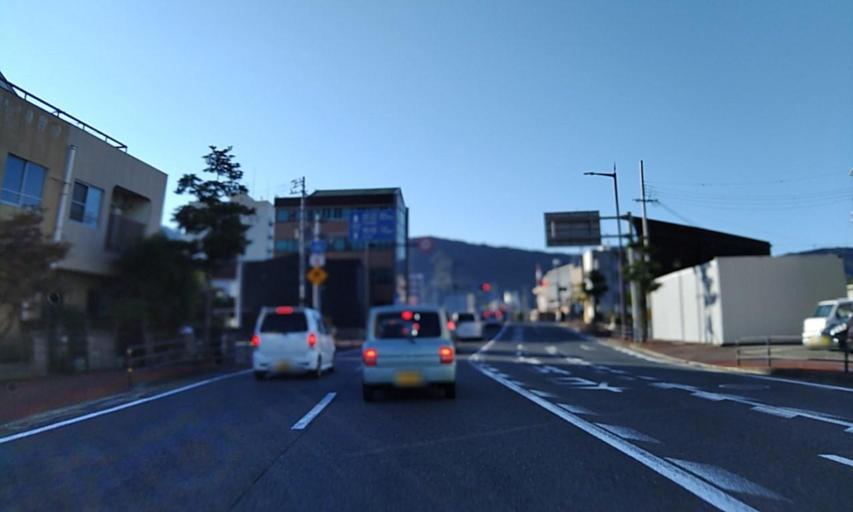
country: JP
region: Wakayama
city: Kainan
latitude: 34.1584
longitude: 135.2056
